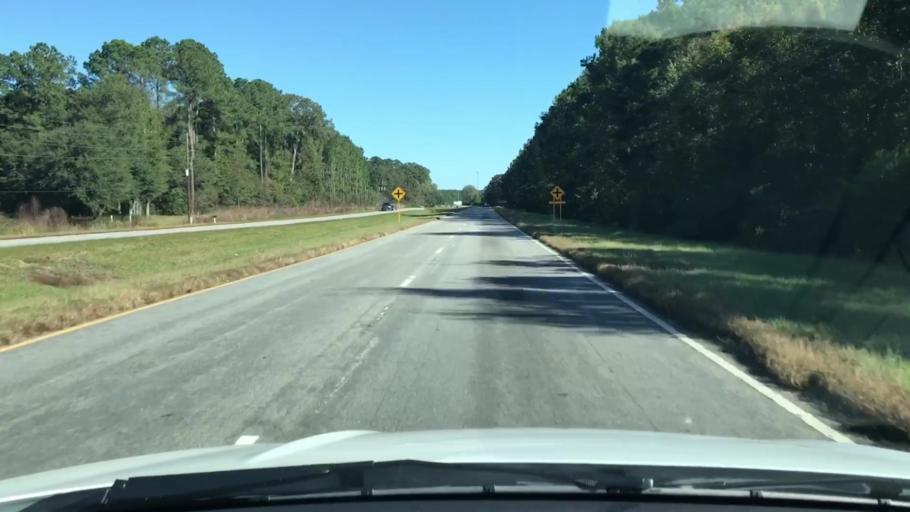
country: US
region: South Carolina
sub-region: Charleston County
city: Ravenel
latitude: 32.7601
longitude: -80.4016
